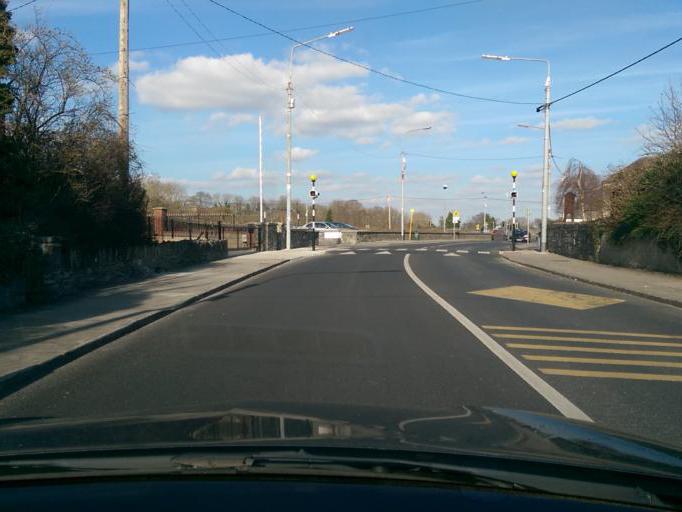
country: IE
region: Leinster
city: Lucan
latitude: 53.3593
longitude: -6.4402
